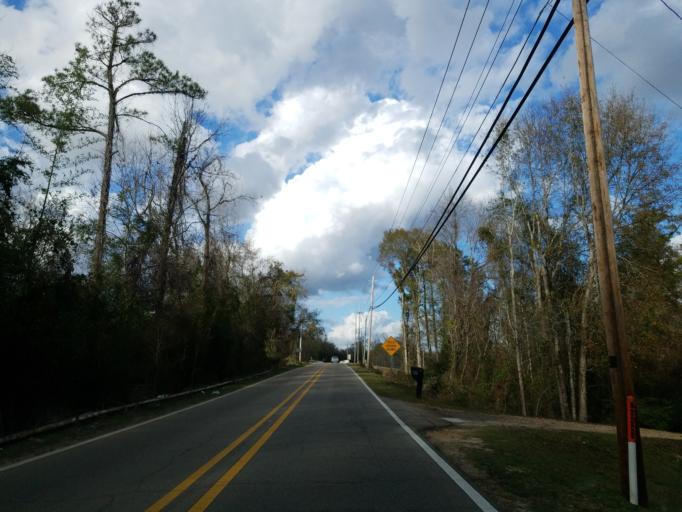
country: US
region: Mississippi
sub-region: Forrest County
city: Glendale
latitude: 31.3475
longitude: -89.3063
